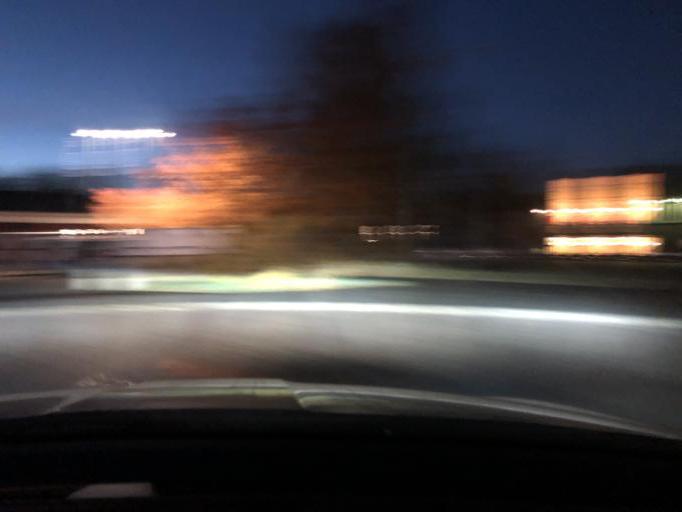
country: SE
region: Stockholm
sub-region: Botkyrka Kommun
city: Alby
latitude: 59.2344
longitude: 17.8472
